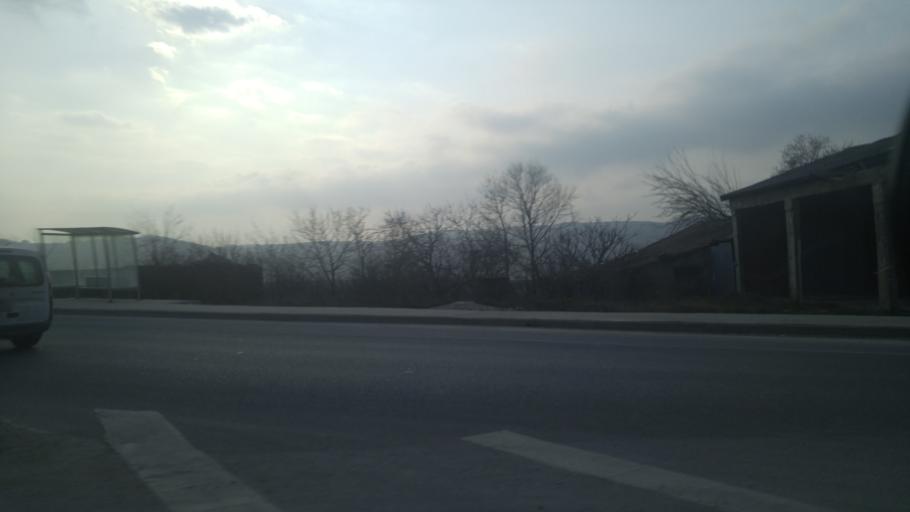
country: TR
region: Istanbul
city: Muratbey
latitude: 41.0891
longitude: 28.5143
